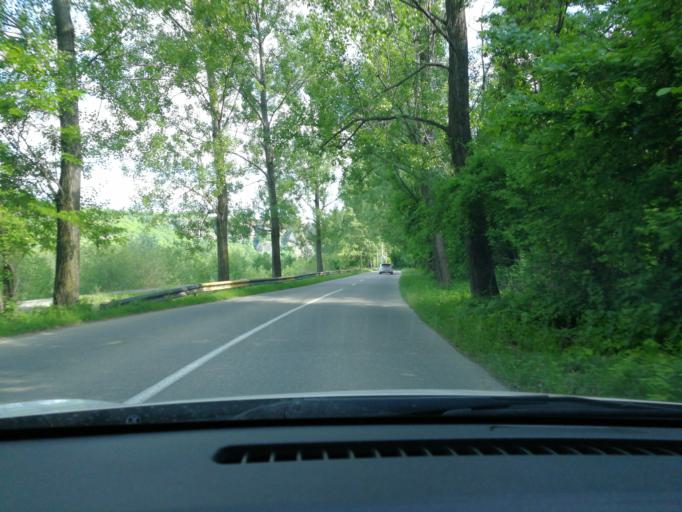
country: RO
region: Prahova
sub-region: Comuna Sotrile
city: Sotrile
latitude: 45.2160
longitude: 25.7384
